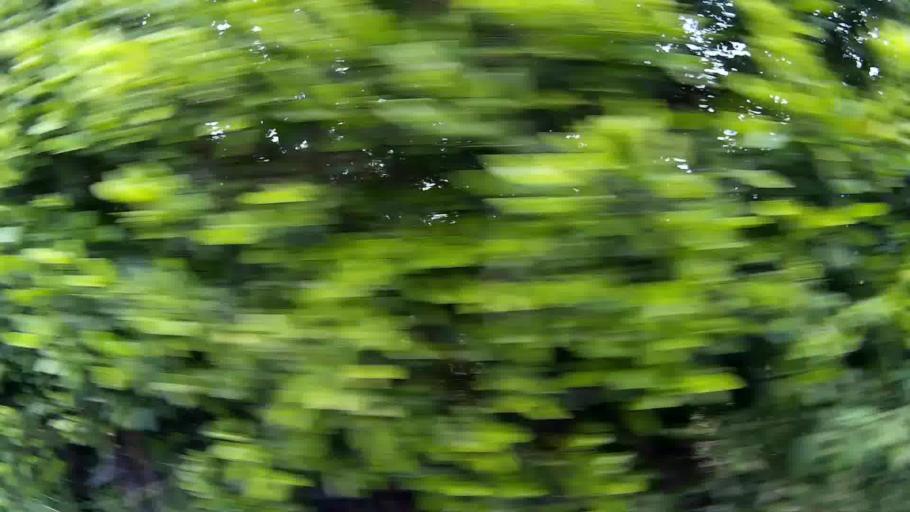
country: CO
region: Risaralda
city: Pereira
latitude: 4.7835
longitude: -75.7228
